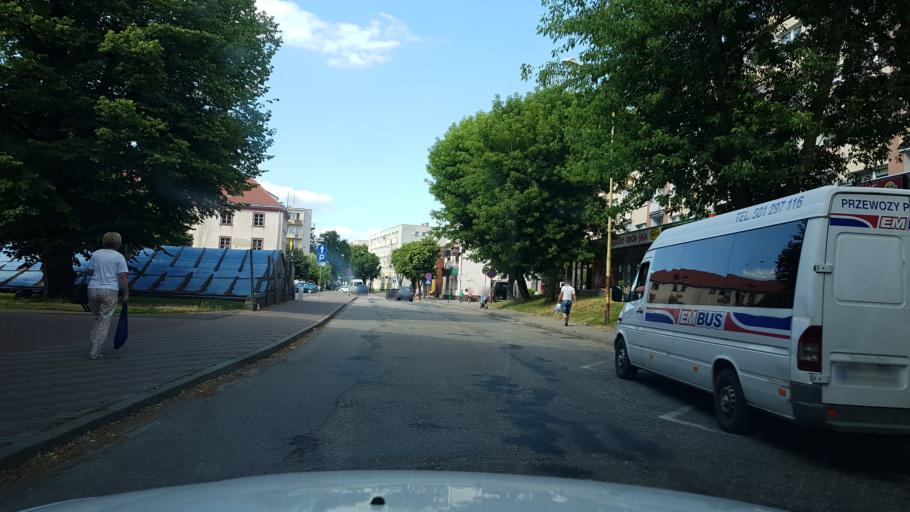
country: PL
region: West Pomeranian Voivodeship
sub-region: Powiat pyrzycki
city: Pyrzyce
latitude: 53.1424
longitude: 14.8936
